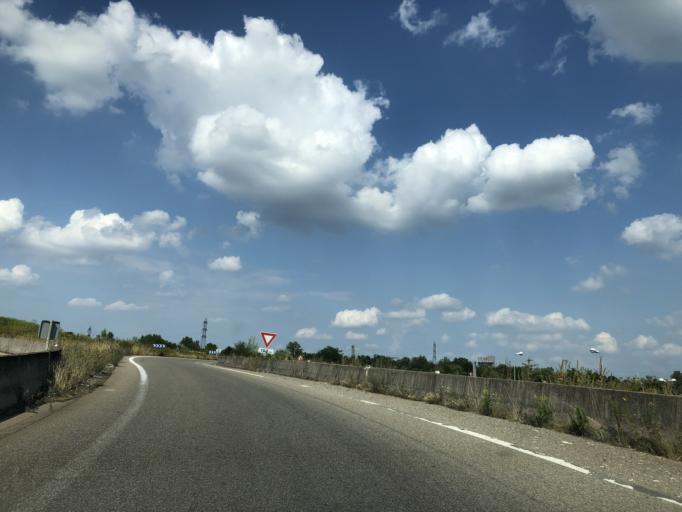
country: FR
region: Alsace
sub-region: Departement du Bas-Rhin
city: Fegersheim
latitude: 48.5071
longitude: 7.6980
